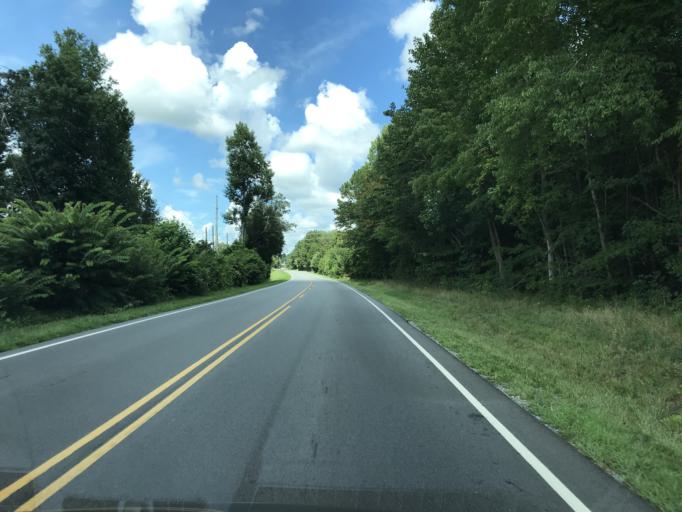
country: US
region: North Carolina
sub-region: Lincoln County
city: Pumpkin Center
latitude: 35.5116
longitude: -81.1565
